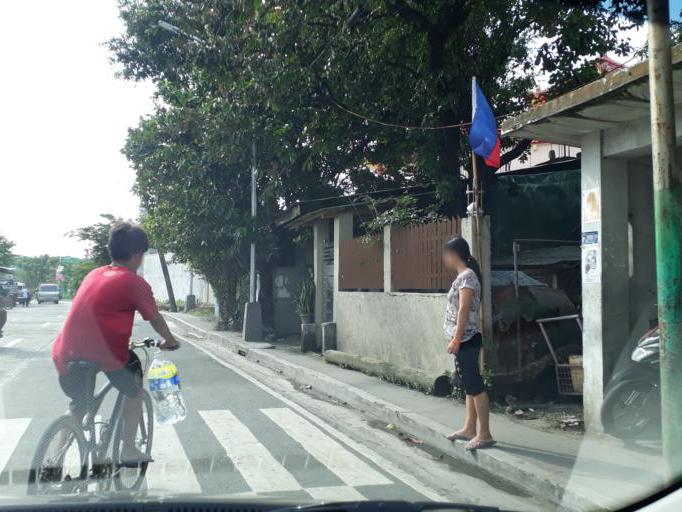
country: PH
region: Metro Manila
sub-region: Caloocan City
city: Niugan
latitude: 14.6700
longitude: 120.9603
